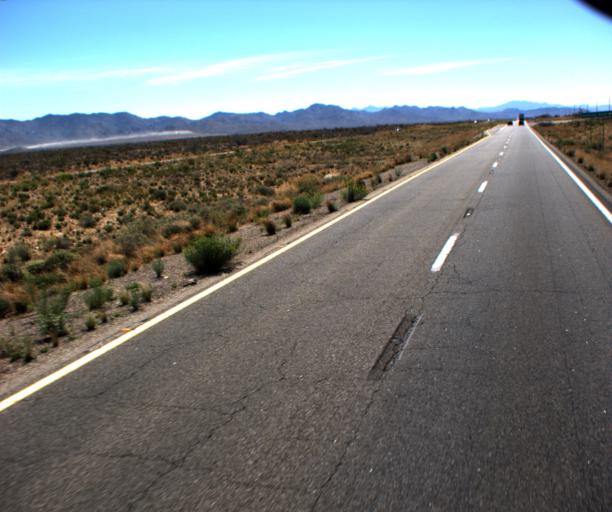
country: US
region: Arizona
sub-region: Mohave County
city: Golden Valley
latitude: 35.3657
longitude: -114.2370
